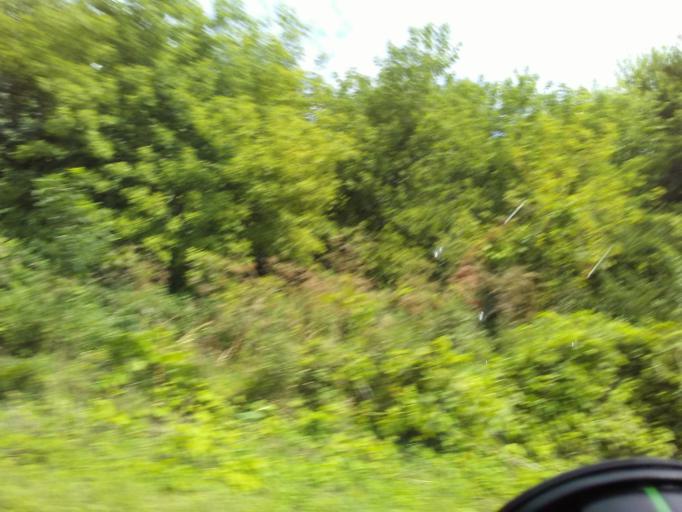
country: US
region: Wisconsin
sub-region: Dane County
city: Verona
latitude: 43.0068
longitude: -89.5780
